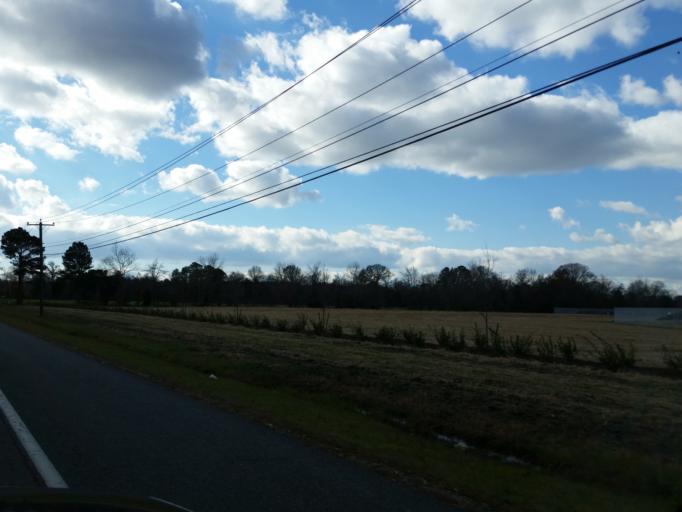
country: US
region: Maryland
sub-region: Talbot County
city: Easton
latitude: 38.7697
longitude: -76.1404
